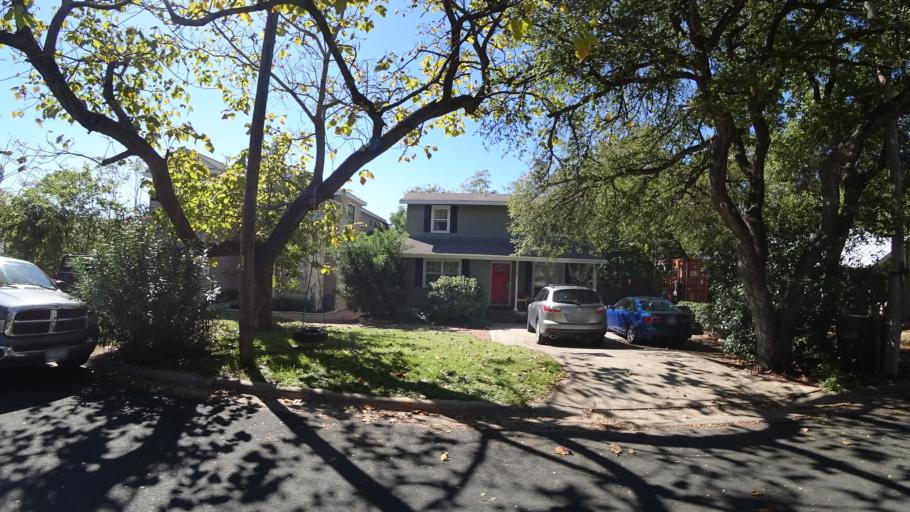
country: US
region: Texas
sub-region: Travis County
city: Austin
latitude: 30.2799
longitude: -97.7073
